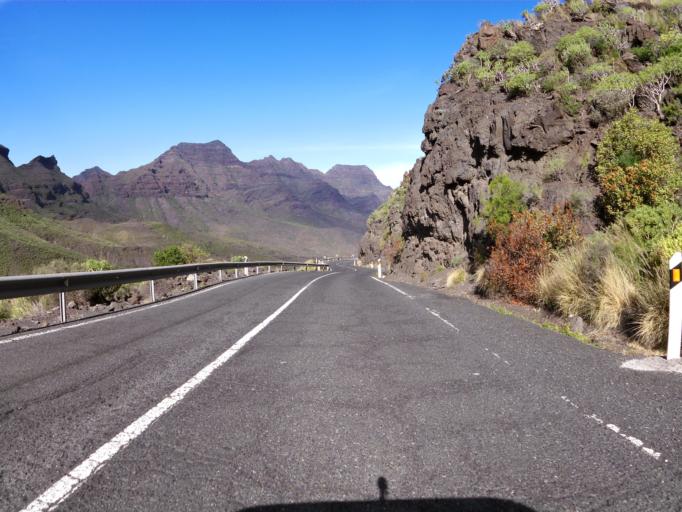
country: ES
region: Canary Islands
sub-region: Provincia de Las Palmas
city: San Nicolas
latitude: 27.9435
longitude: -15.7595
